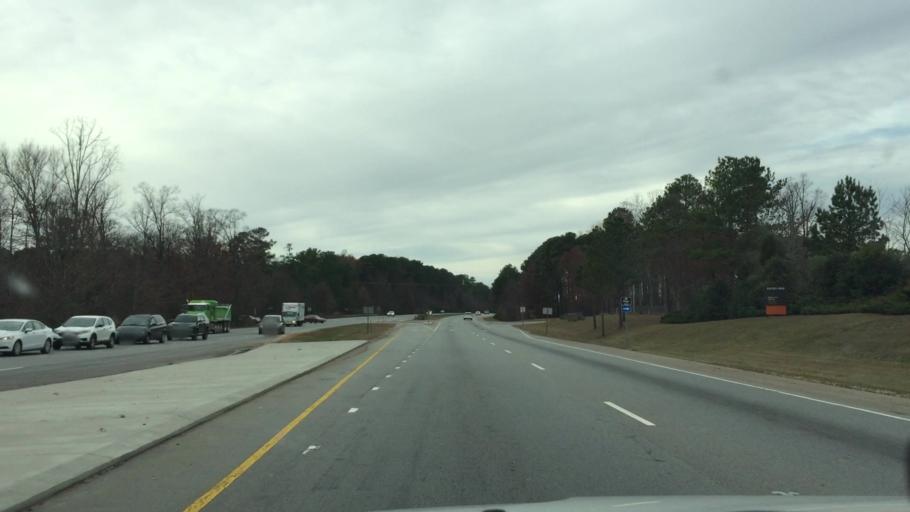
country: US
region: North Carolina
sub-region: Wake County
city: Apex
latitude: 35.7439
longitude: -78.8222
